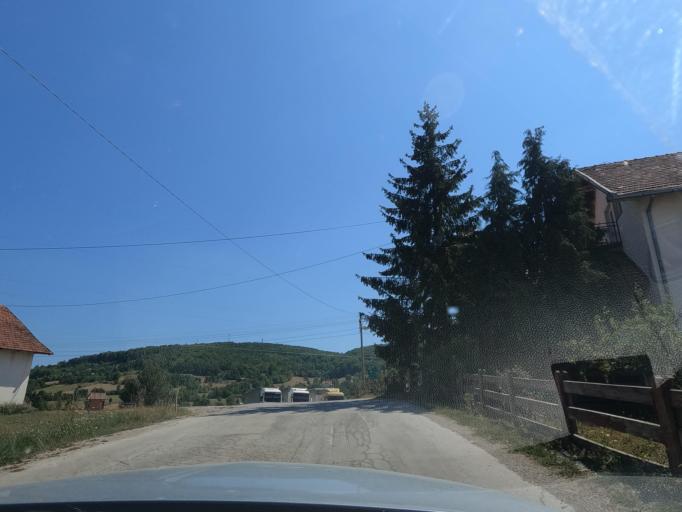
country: RS
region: Central Serbia
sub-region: Zlatiborski Okrug
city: Cajetina
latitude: 43.7891
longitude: 19.7657
